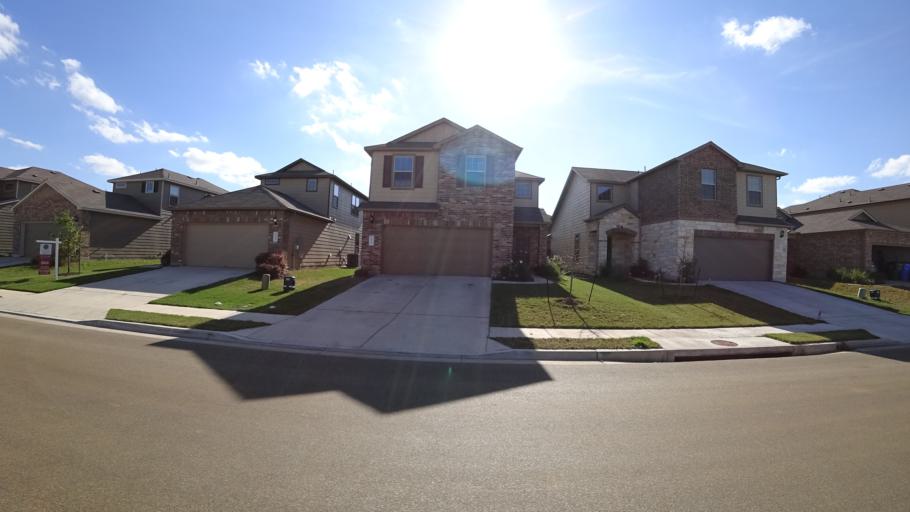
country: US
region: Texas
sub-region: Travis County
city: Wells Branch
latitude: 30.4700
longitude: -97.6814
